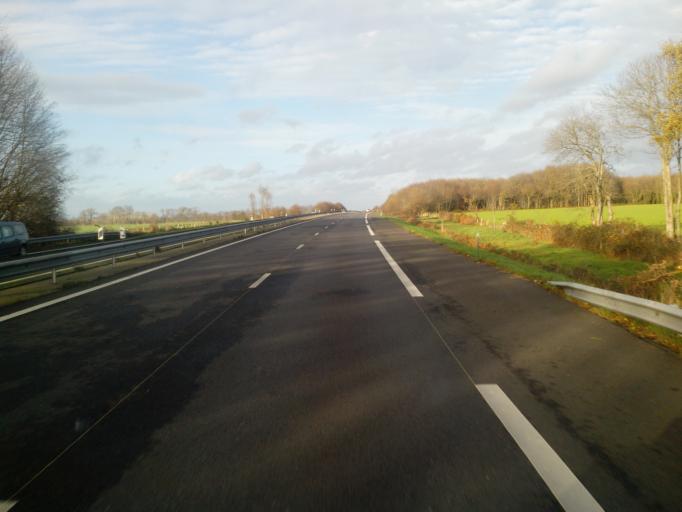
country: FR
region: Brittany
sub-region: Departement d'Ille-et-Vilaine
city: Tinteniac
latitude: 48.3410
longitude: -1.8619
